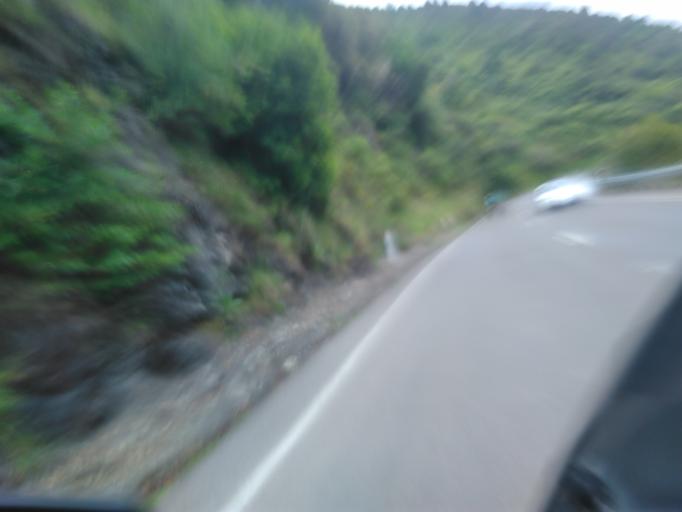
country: NZ
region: Bay of Plenty
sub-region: Opotiki District
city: Opotiki
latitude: -38.2416
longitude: 177.3117
